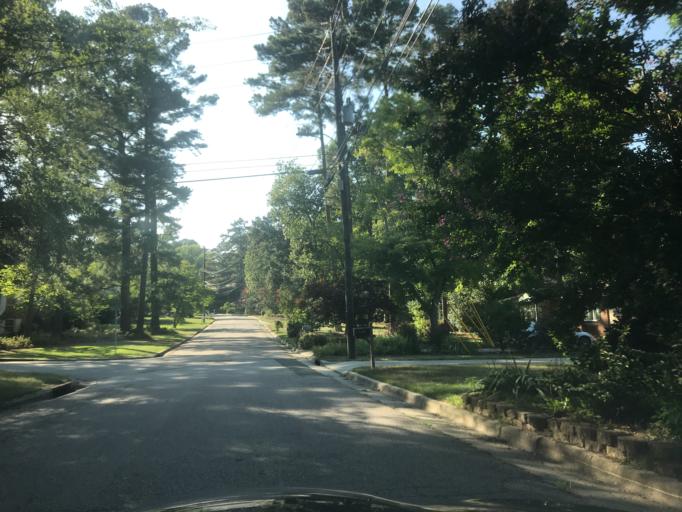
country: US
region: North Carolina
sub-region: Wake County
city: West Raleigh
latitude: 35.8459
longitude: -78.6350
